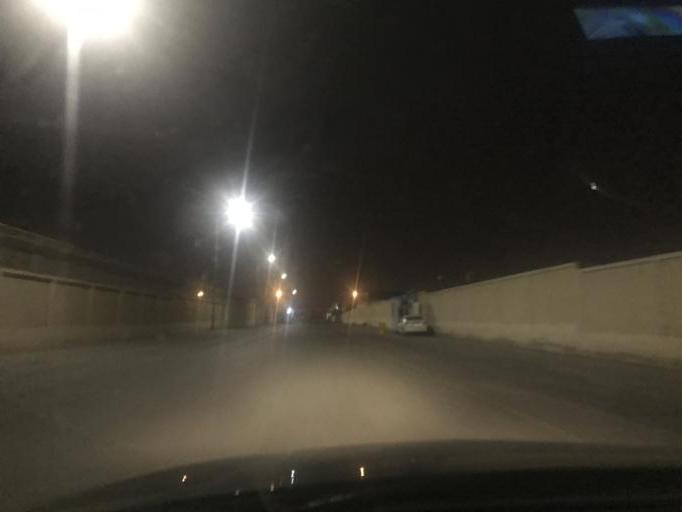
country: SA
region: Ar Riyad
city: Riyadh
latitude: 24.7233
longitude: 46.7842
